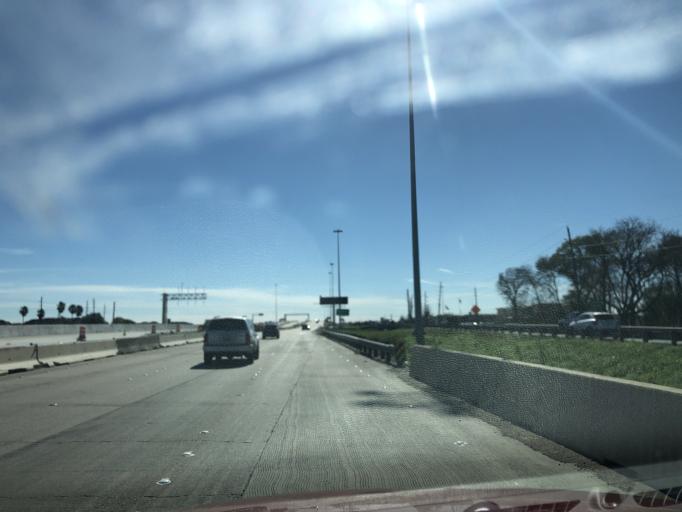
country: US
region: Texas
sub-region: Brazoria County
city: Brookside Village
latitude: 29.5869
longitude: -95.3866
